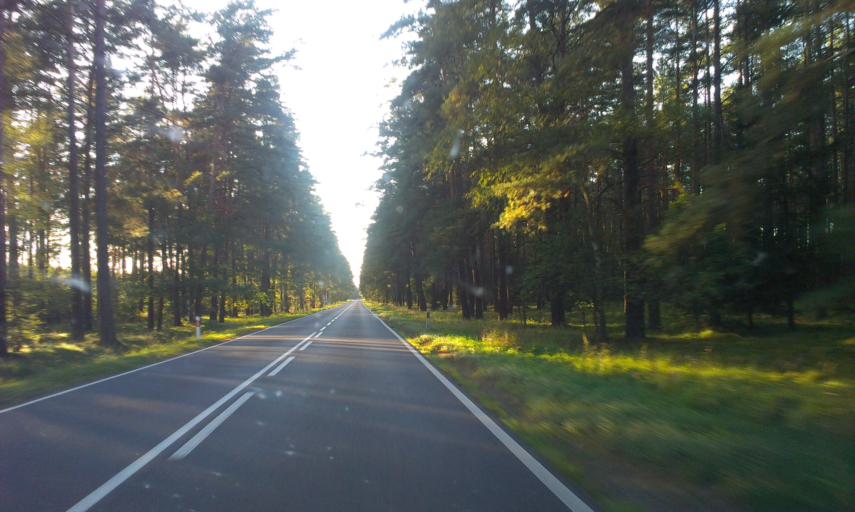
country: PL
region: Pomeranian Voivodeship
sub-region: Powiat czluchowski
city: Czarne
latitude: 53.7019
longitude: 16.8773
